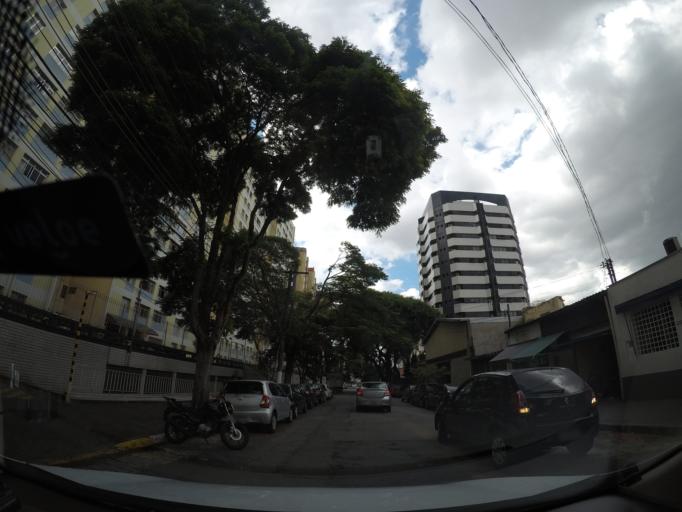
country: BR
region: Sao Paulo
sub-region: Sao Paulo
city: Sao Paulo
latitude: -23.6173
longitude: -46.6376
